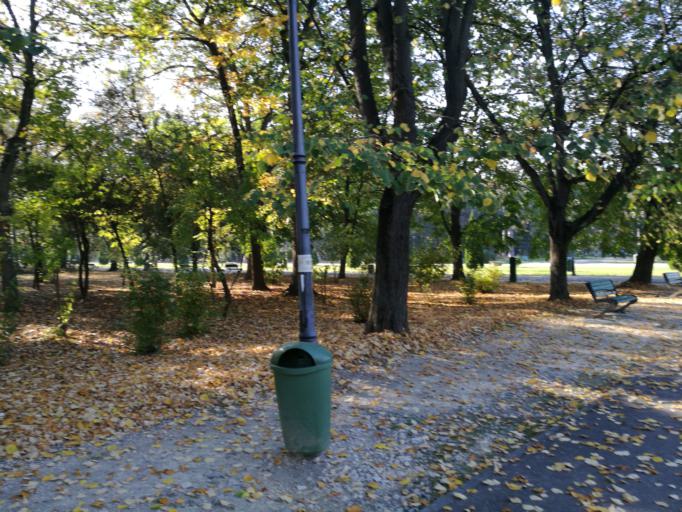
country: RO
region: Bucuresti
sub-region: Municipiul Bucuresti
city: Bucharest
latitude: 44.4807
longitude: 26.0846
